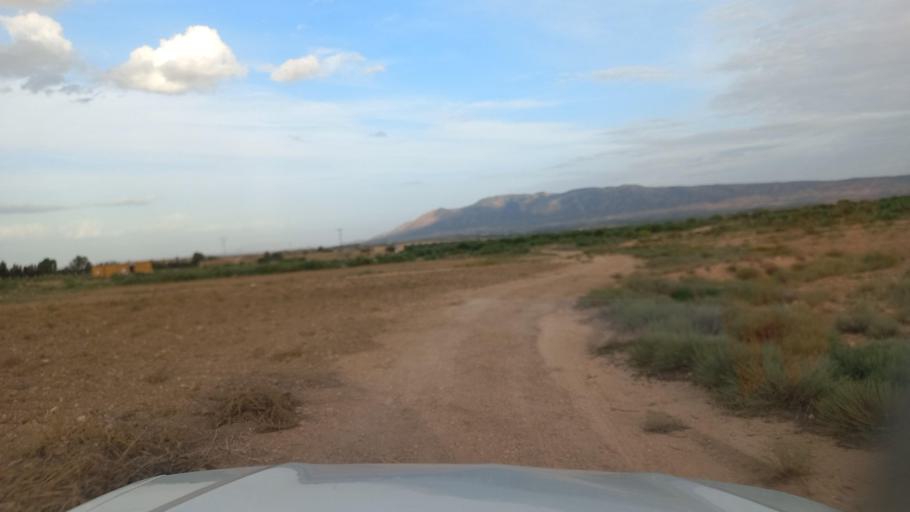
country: TN
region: Al Qasrayn
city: Sbiba
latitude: 35.4394
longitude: 9.0891
